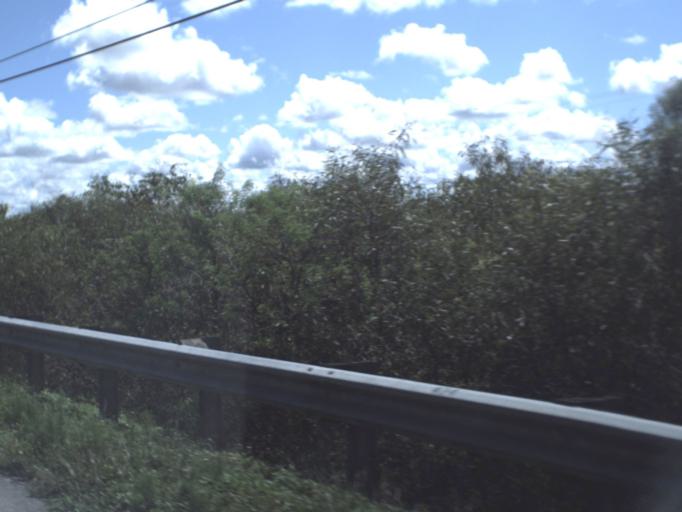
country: US
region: Florida
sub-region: Highlands County
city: Lake Placid
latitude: 27.2088
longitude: -81.2291
